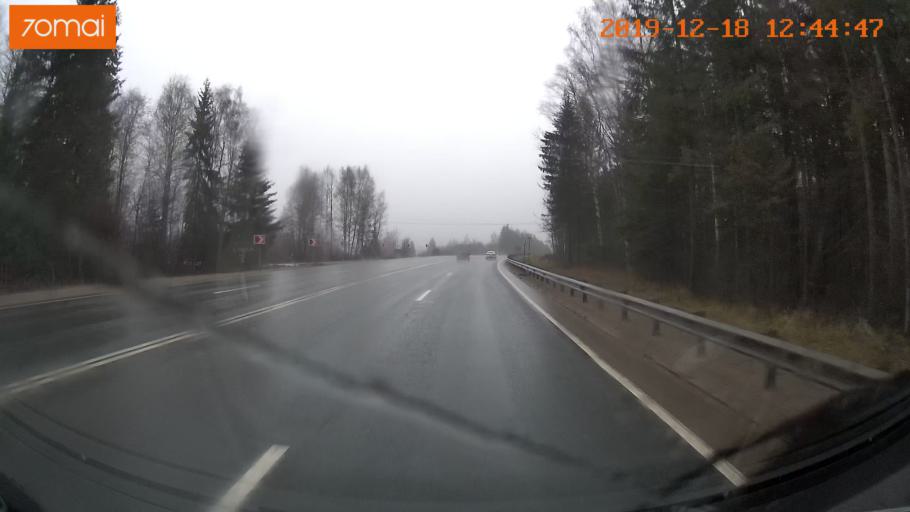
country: RU
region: Moskovskaya
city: Klin
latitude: 56.2241
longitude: 36.6509
